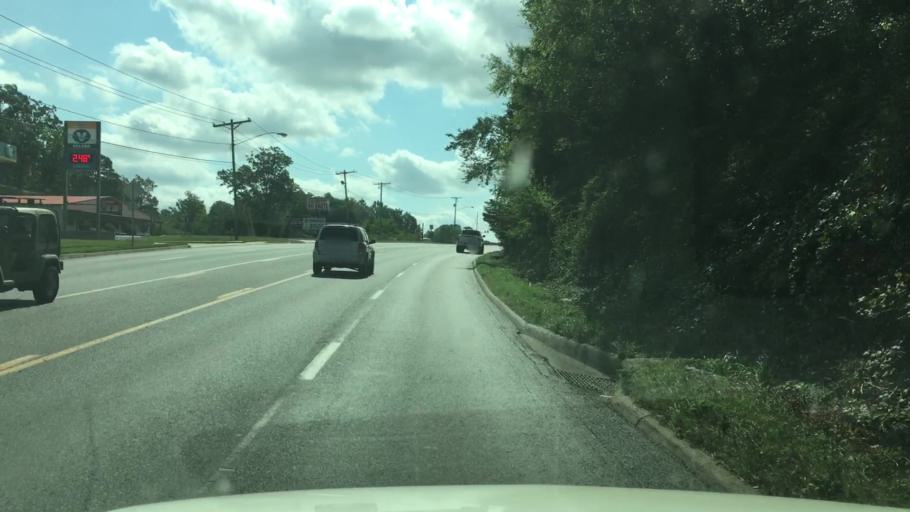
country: US
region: Arkansas
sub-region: Garland County
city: Piney
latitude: 34.4943
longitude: -93.1185
